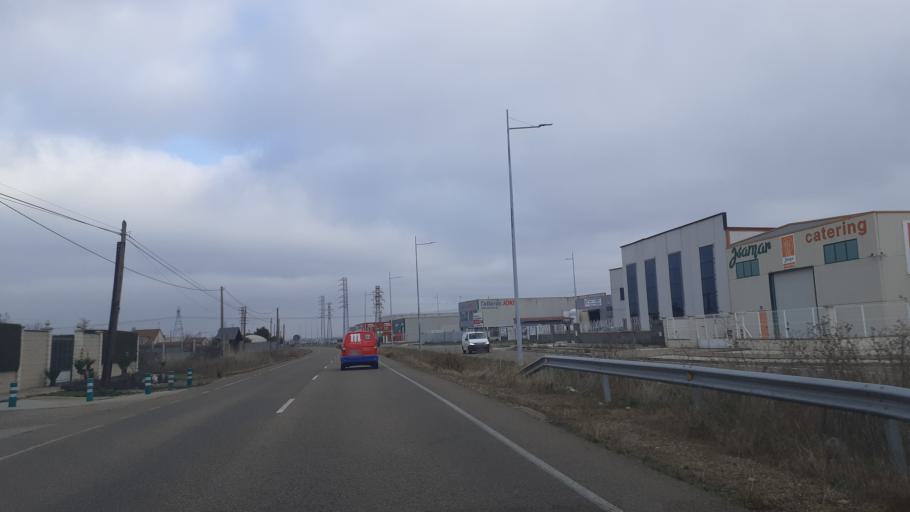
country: ES
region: Castille and Leon
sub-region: Provincia de Leon
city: Onzonilla
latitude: 42.5493
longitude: -5.5860
